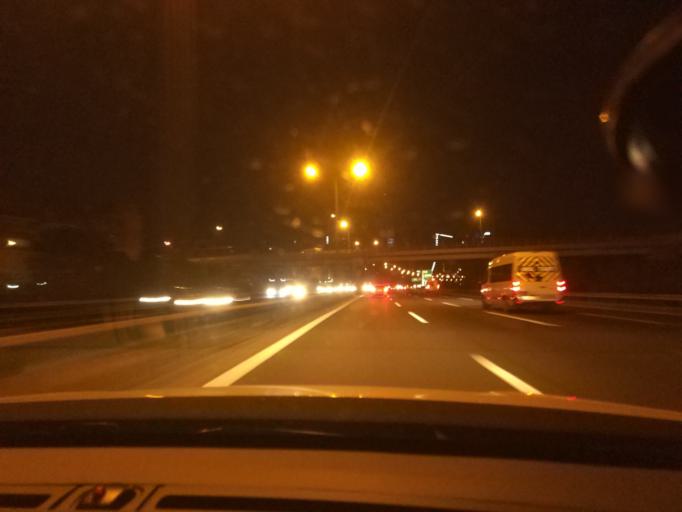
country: TR
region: Istanbul
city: Umraniye
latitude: 41.0112
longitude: 29.1218
